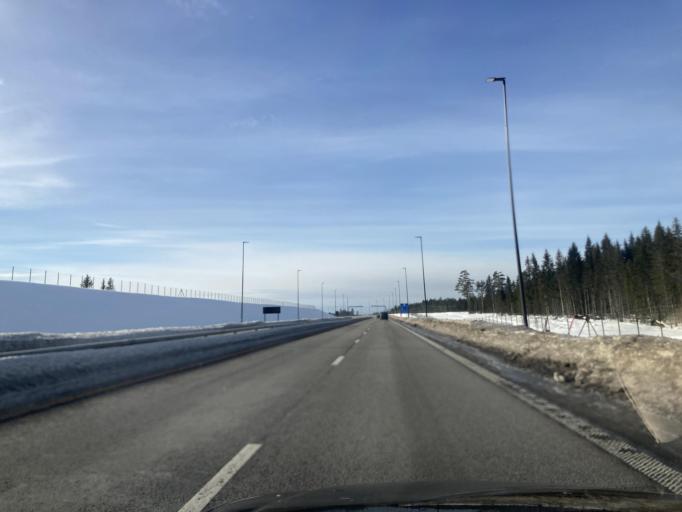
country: NO
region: Hedmark
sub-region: Elverum
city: Elverum
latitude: 60.8789
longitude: 11.4608
